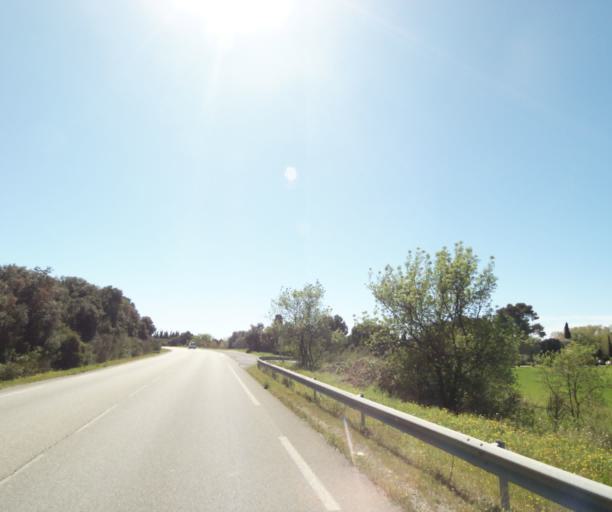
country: FR
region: Languedoc-Roussillon
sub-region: Departement de l'Herault
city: Villeneuve-les-Maguelone
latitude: 43.5586
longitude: 3.8519
